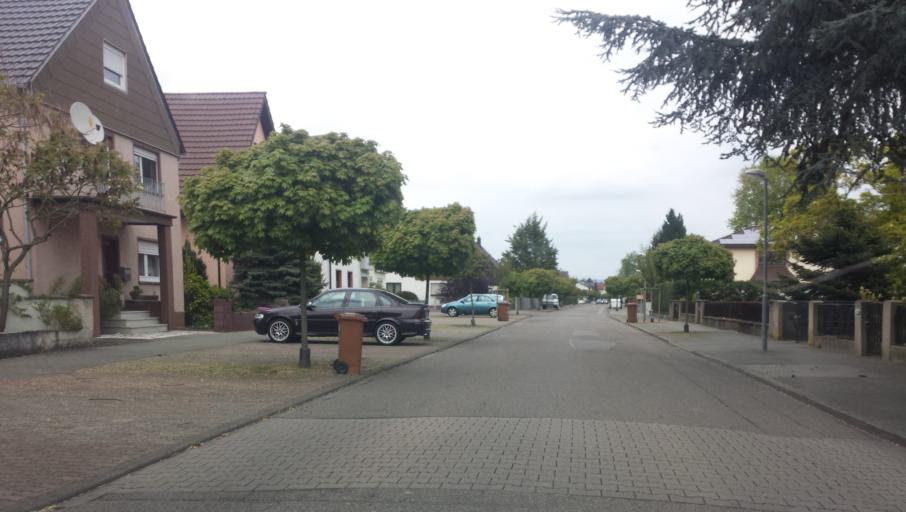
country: DE
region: Baden-Wuerttemberg
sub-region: Karlsruhe Region
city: Ketsch
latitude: 49.3622
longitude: 8.5308
